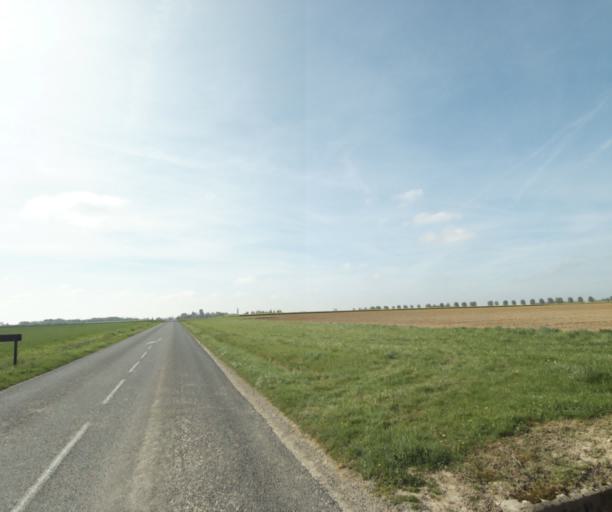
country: FR
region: Ile-de-France
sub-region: Departement de Seine-et-Marne
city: Bailly-Carrois
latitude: 48.5785
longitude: 3.0117
